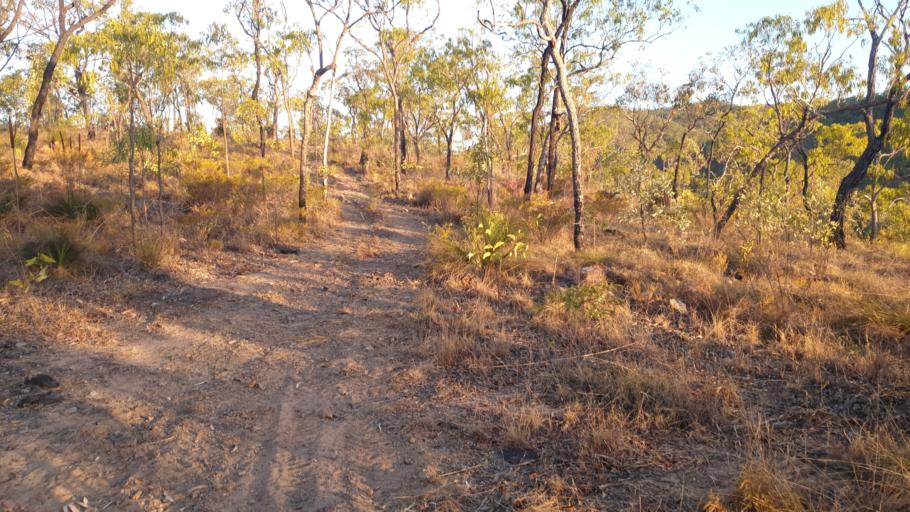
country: AU
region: Queensland
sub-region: Tablelands
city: Atherton
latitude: -17.4017
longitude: 145.2272
